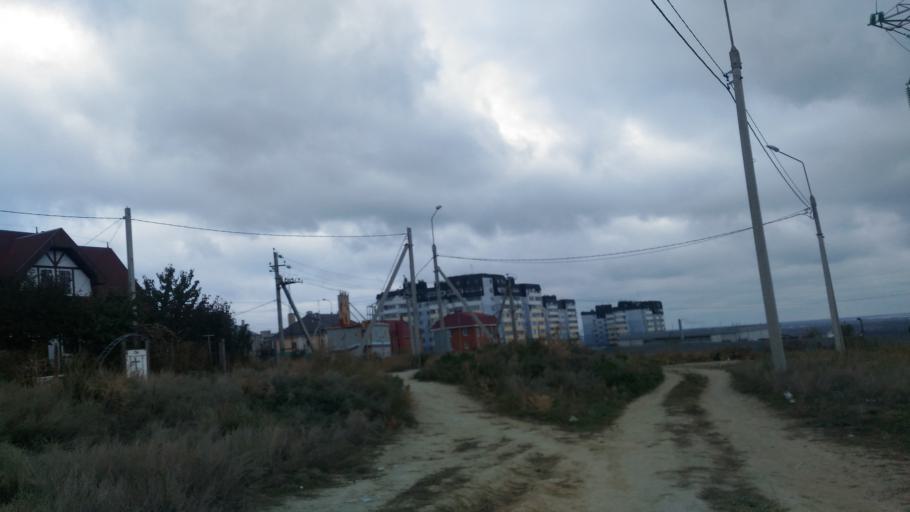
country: RU
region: Volgograd
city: Volgograd
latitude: 48.6448
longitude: 44.4260
